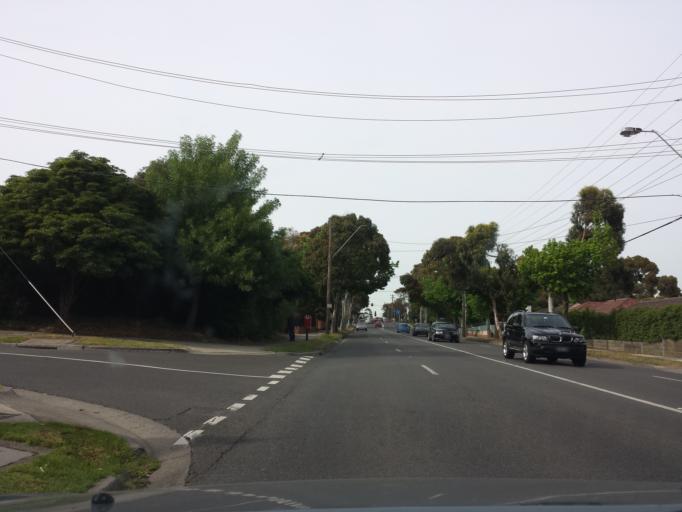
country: AU
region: Victoria
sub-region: Monash
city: Ashwood
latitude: -37.8729
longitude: 145.1296
